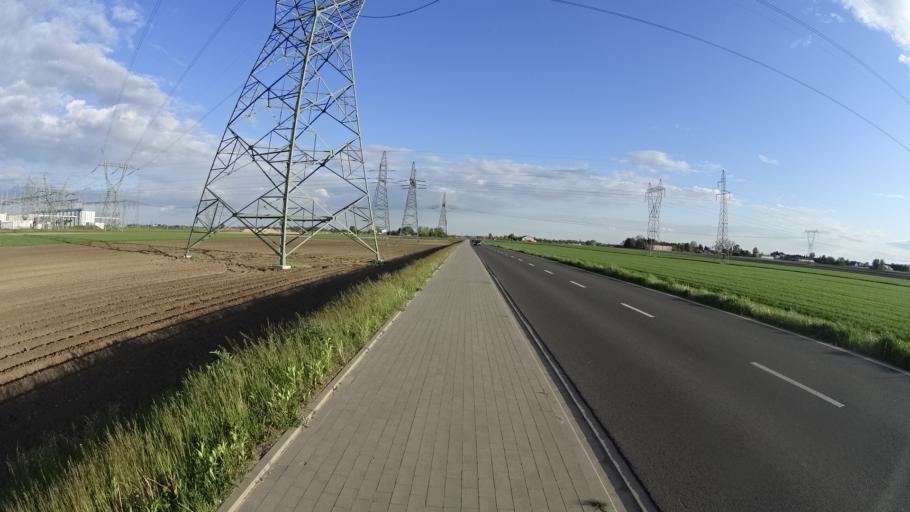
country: PL
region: Masovian Voivodeship
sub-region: Powiat warszawski zachodni
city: Jozefow
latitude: 52.2287
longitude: 20.7377
